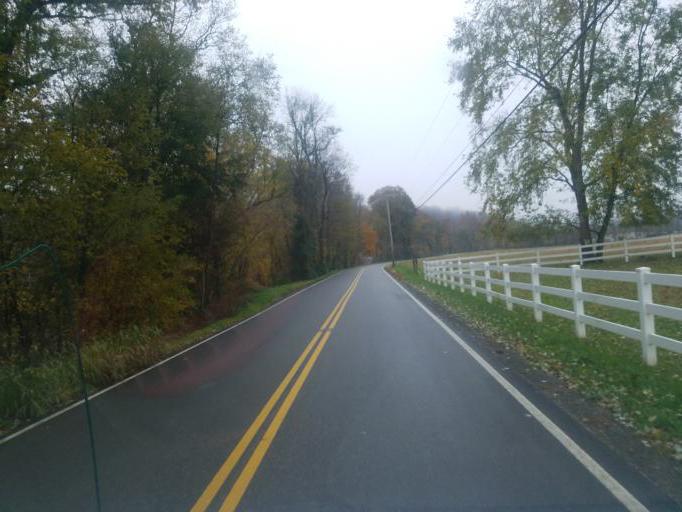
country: US
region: Ohio
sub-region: Morgan County
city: McConnelsville
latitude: 39.6349
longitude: -81.8391
